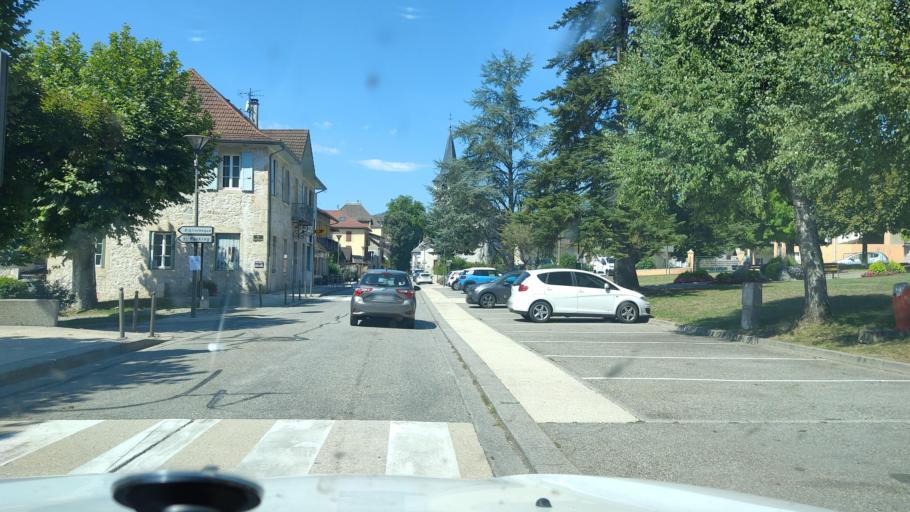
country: FR
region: Rhone-Alpes
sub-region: Departement de la Savoie
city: Novalaise
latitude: 45.5947
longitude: 5.7730
